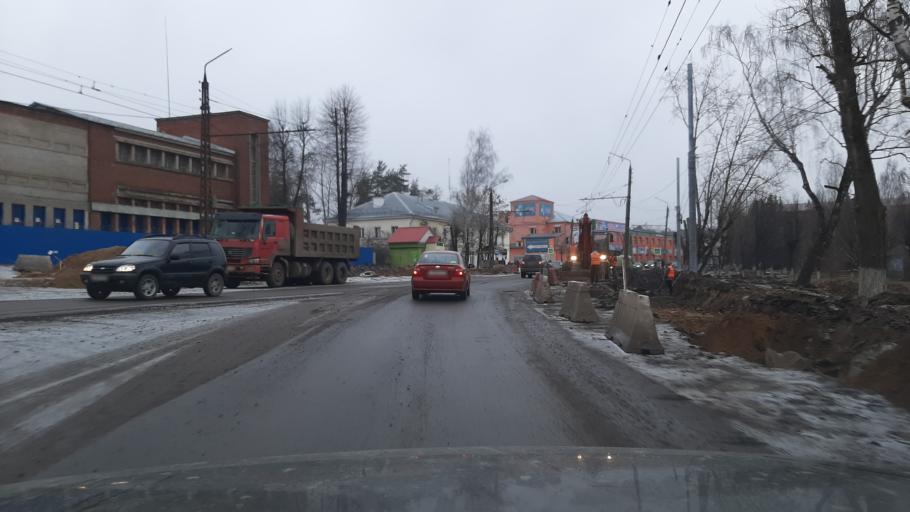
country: RU
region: Ivanovo
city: Kokhma
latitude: 56.9293
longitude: 41.0849
